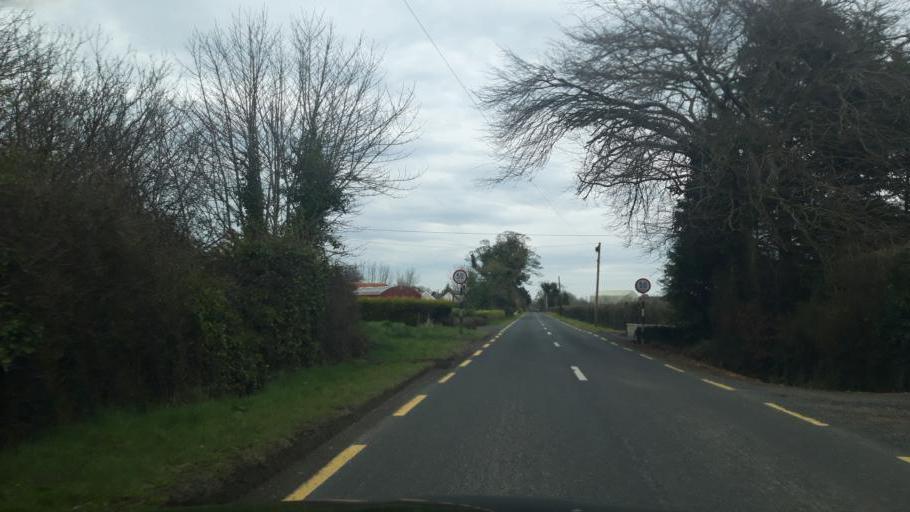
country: IE
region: Leinster
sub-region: Kildare
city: Clane
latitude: 53.3305
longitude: -6.6856
